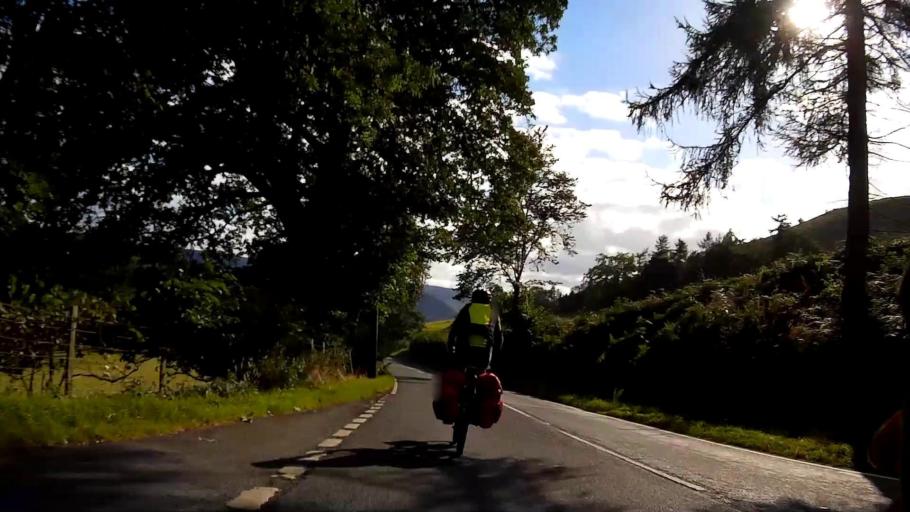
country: GB
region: Wales
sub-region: Denbighshire
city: Llangollen
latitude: 53.0018
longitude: -3.1919
